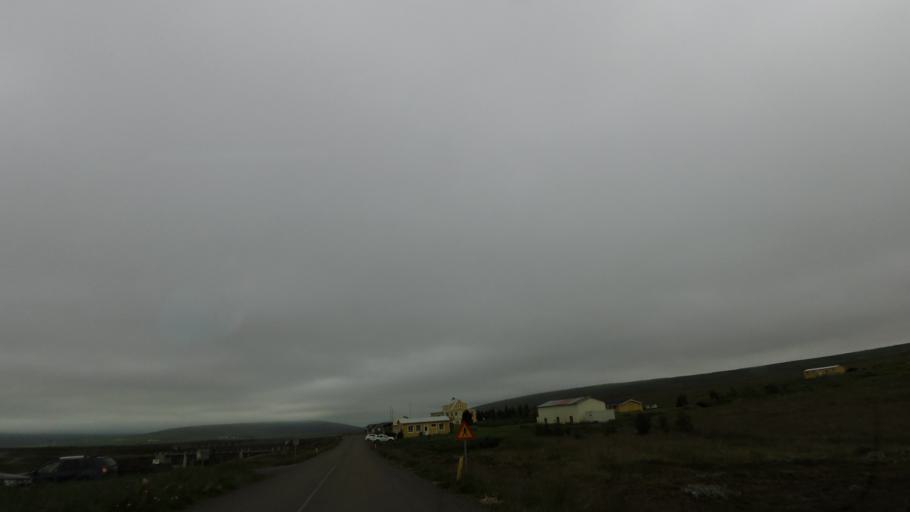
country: IS
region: Northeast
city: Laugar
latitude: 65.6837
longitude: -17.5402
